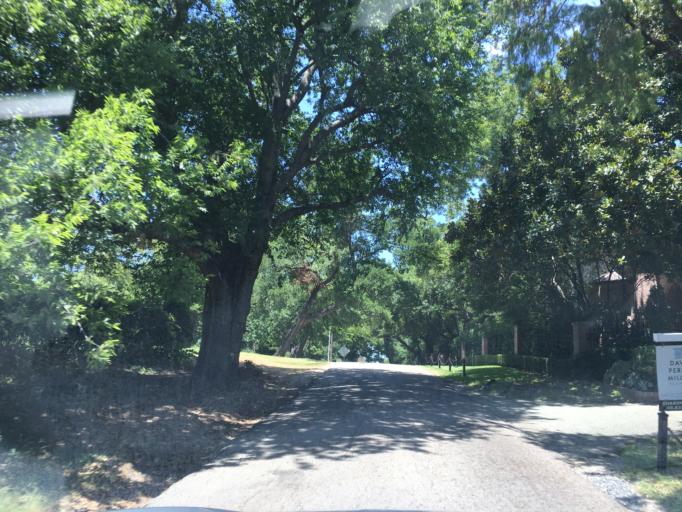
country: US
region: Texas
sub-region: Dallas County
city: Highland Park
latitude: 32.8349
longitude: -96.7280
